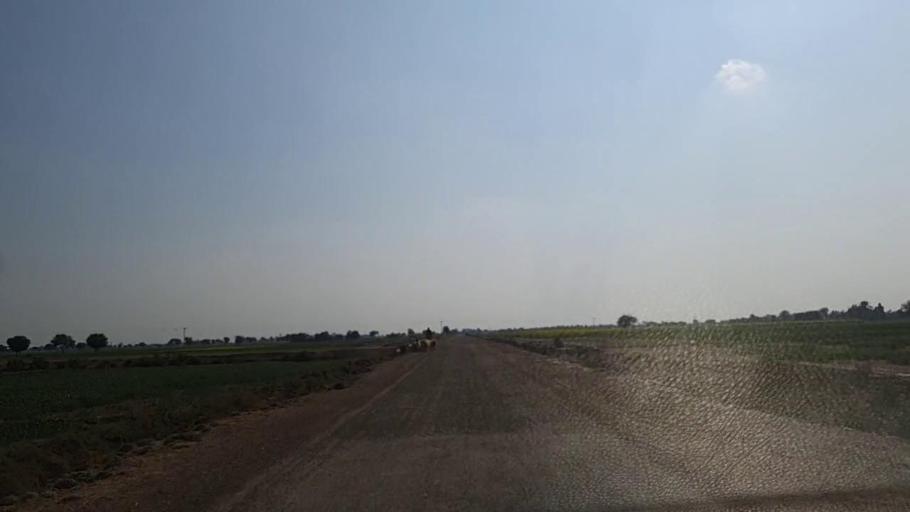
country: PK
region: Sindh
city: Jam Sahib
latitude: 26.2550
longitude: 68.5669
